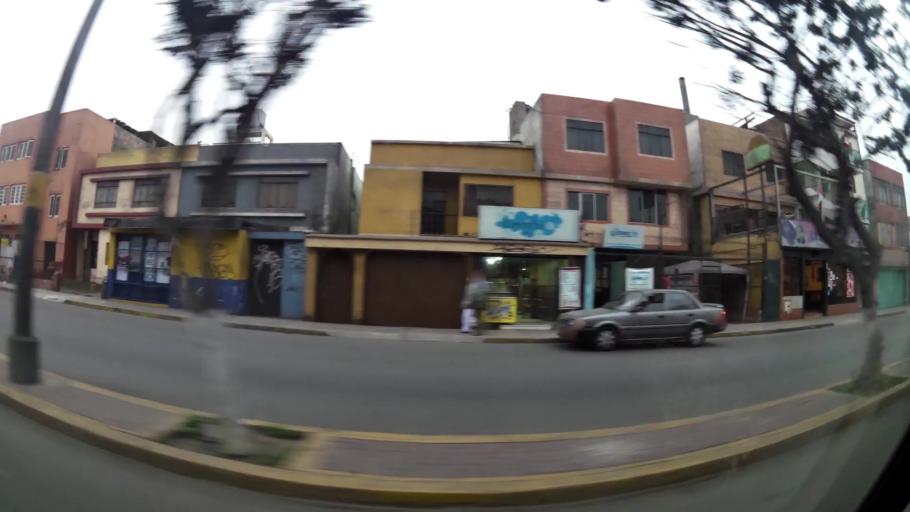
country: PE
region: Lima
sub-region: Lima
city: San Isidro
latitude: -12.0806
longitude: -77.0663
